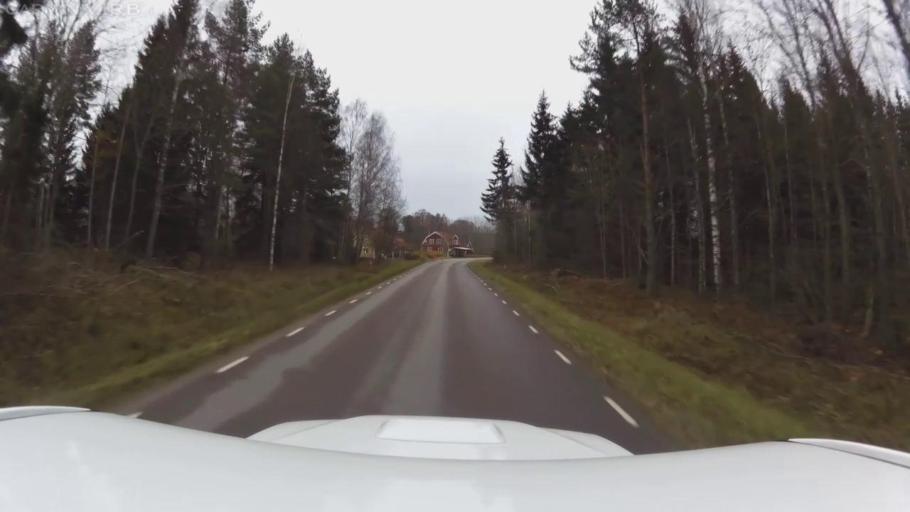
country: SE
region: OEstergoetland
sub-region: Linkopings Kommun
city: Vikingstad
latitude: 58.2332
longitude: 15.3933
